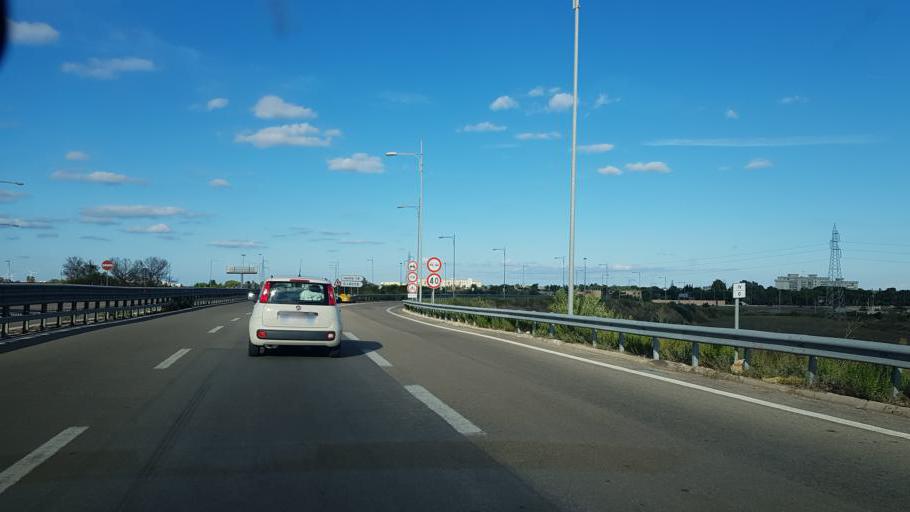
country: IT
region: Apulia
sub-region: Provincia di Lecce
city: Giorgilorio
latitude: 40.3694
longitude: 18.1457
